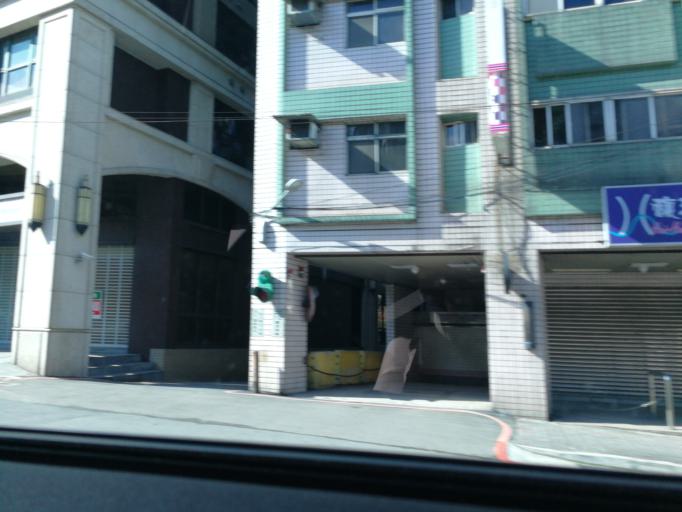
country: TW
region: Taipei
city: Taipei
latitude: 24.9559
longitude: 121.5386
